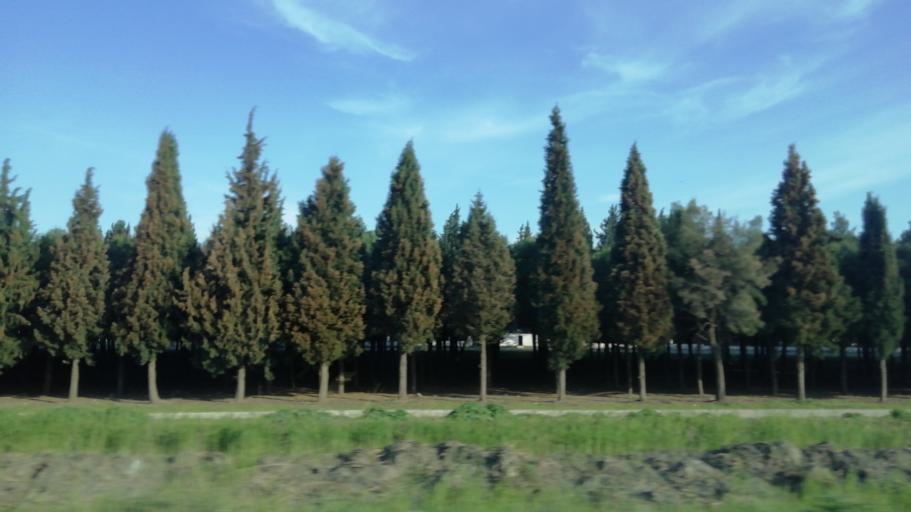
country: TR
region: Manisa
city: Saruhanli
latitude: 38.7466
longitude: 27.6148
